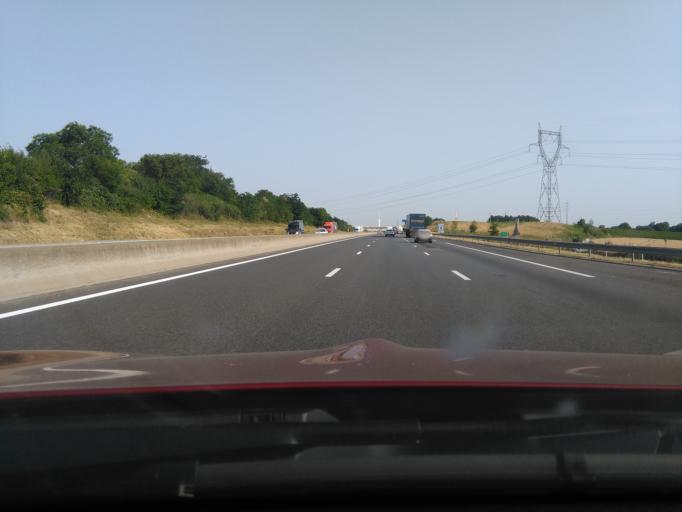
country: FR
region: Rhone-Alpes
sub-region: Departement du Rhone
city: Montanay
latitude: 45.8910
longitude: 4.8917
